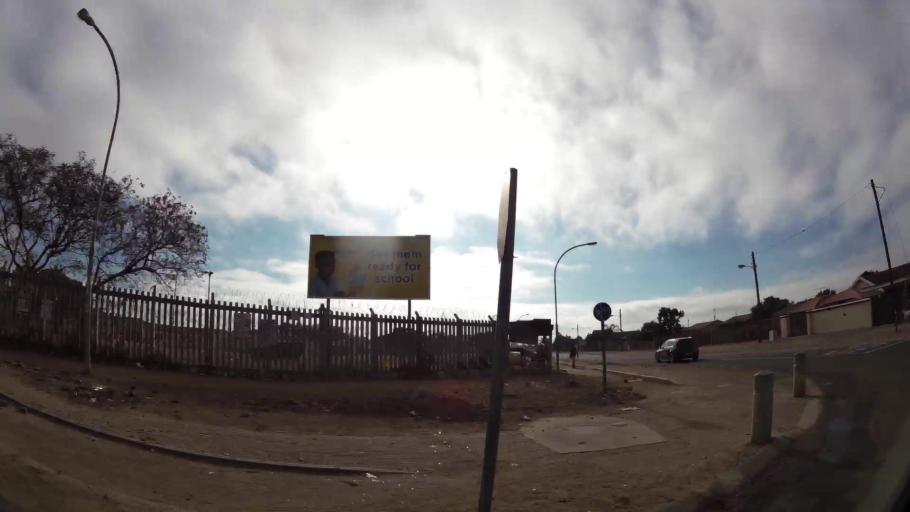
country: ZA
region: Limpopo
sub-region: Capricorn District Municipality
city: Polokwane
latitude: -23.8444
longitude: 29.3893
